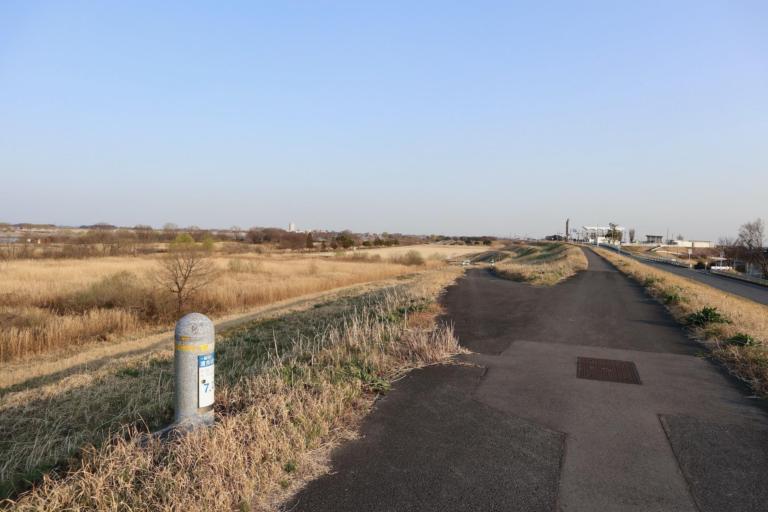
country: JP
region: Tochigi
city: Fujioka
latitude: 36.2141
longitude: 139.6603
